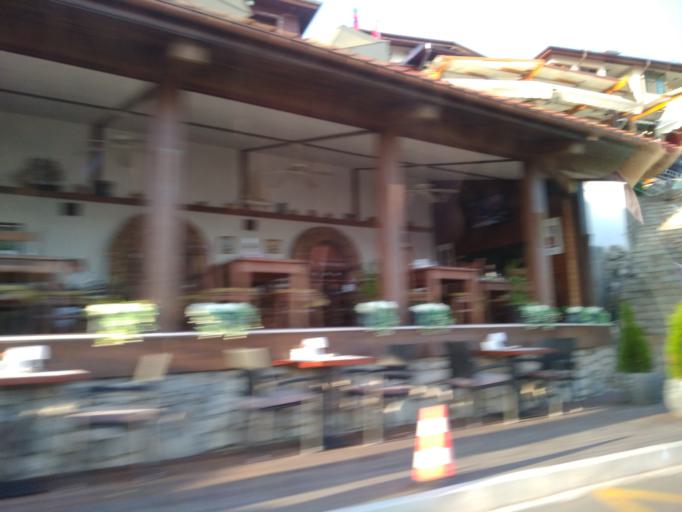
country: BG
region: Burgas
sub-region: Obshtina Nesebur
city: Nesebar
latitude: 42.6578
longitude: 27.7318
